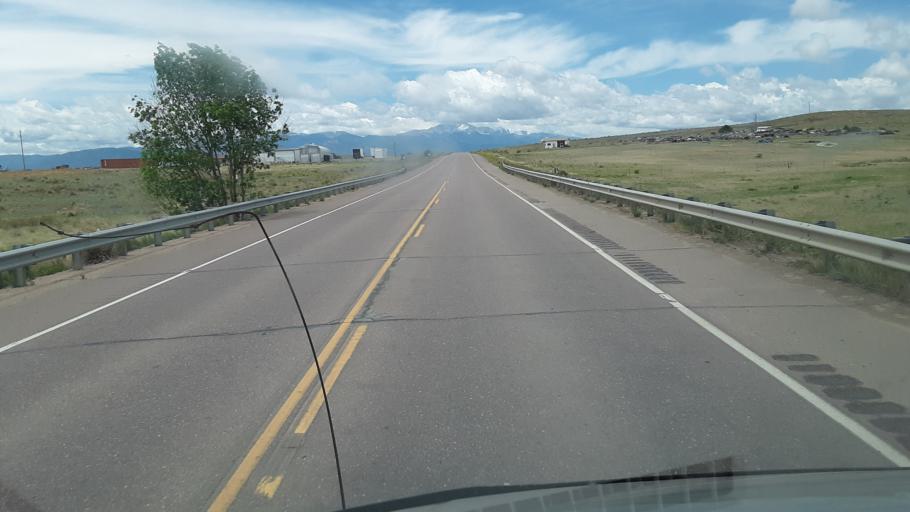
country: US
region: Colorado
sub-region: El Paso County
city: Cimarron Hills
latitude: 38.8387
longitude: -104.5976
